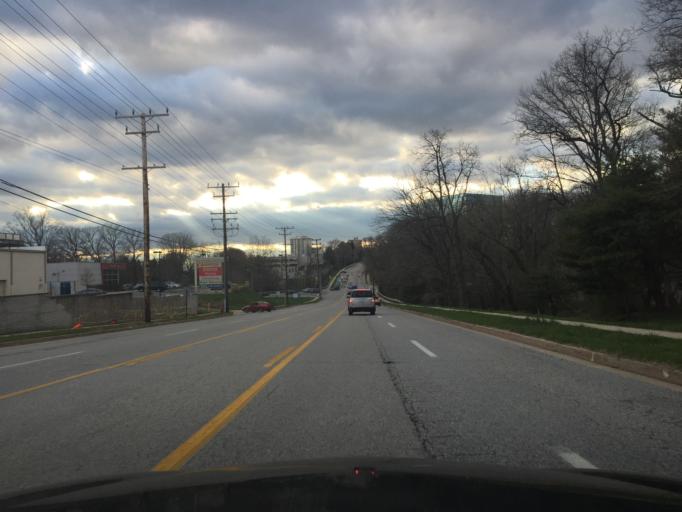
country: US
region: Maryland
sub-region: Baltimore County
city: Towson
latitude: 39.3985
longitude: -76.5842
